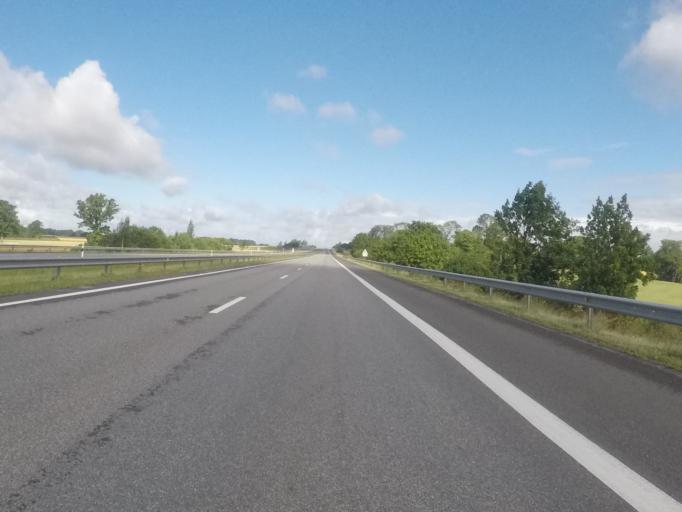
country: LT
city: Ariogala
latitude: 55.2891
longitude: 23.2933
